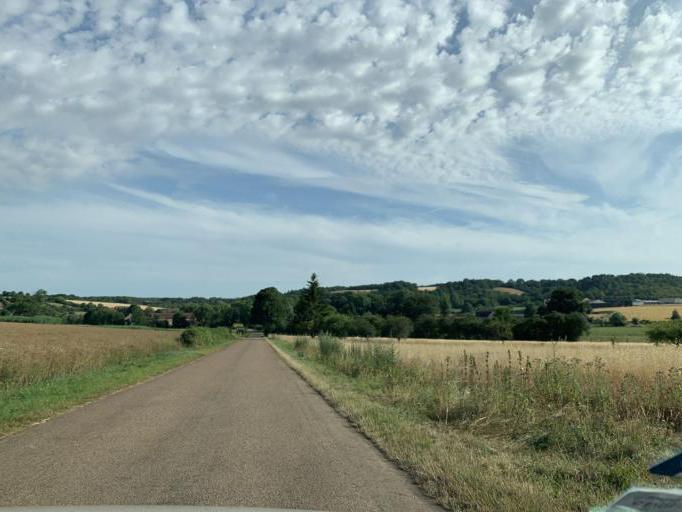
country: FR
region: Bourgogne
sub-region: Departement de l'Yonne
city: Fontenailles
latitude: 47.4766
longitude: 3.4220
